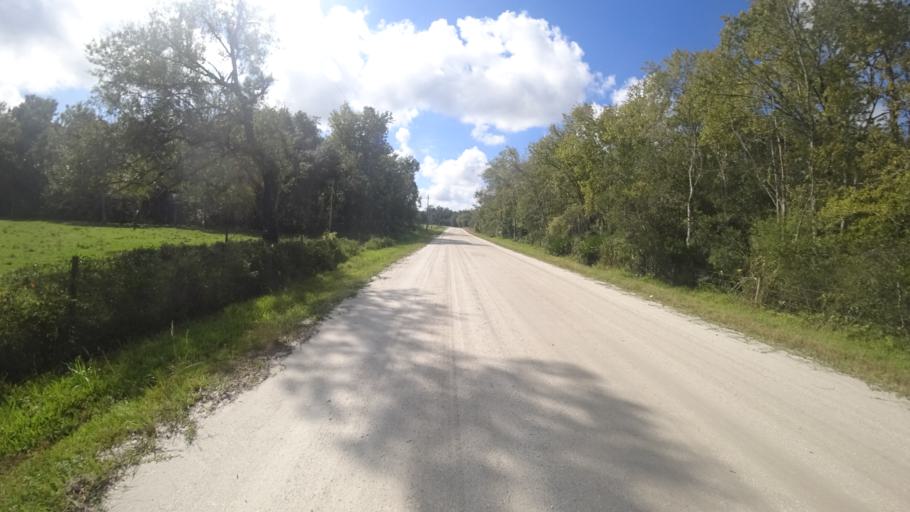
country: US
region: Florida
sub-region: Sarasota County
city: Lake Sarasota
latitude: 27.3383
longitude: -82.2051
